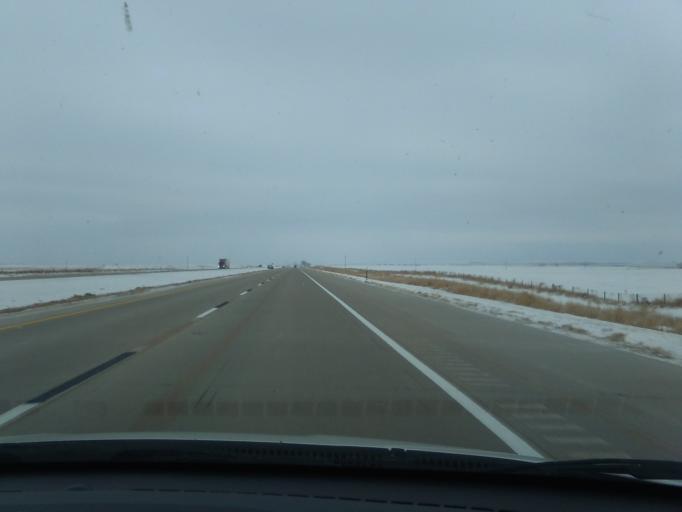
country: US
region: Colorado
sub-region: Sedgwick County
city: Julesburg
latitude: 41.0425
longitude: -102.2536
